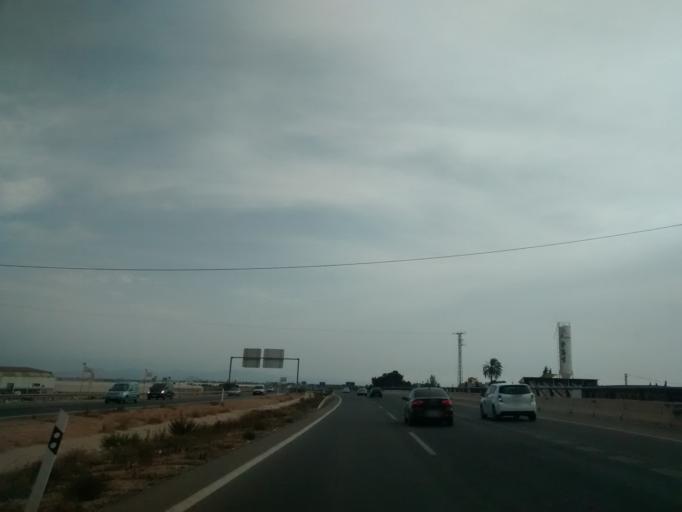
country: ES
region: Murcia
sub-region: Murcia
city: San Javier
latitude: 37.7866
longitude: -0.8402
